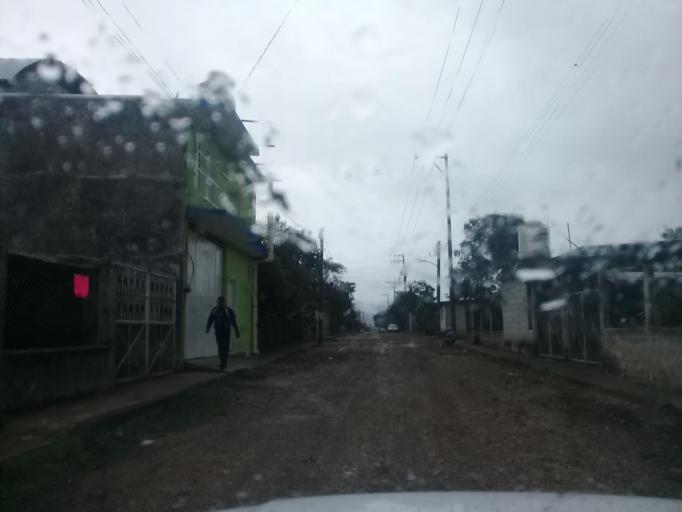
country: MX
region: Veracruz
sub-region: Amatlan de los Reyes
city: Trapiche Viejo
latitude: 18.8433
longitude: -96.9441
